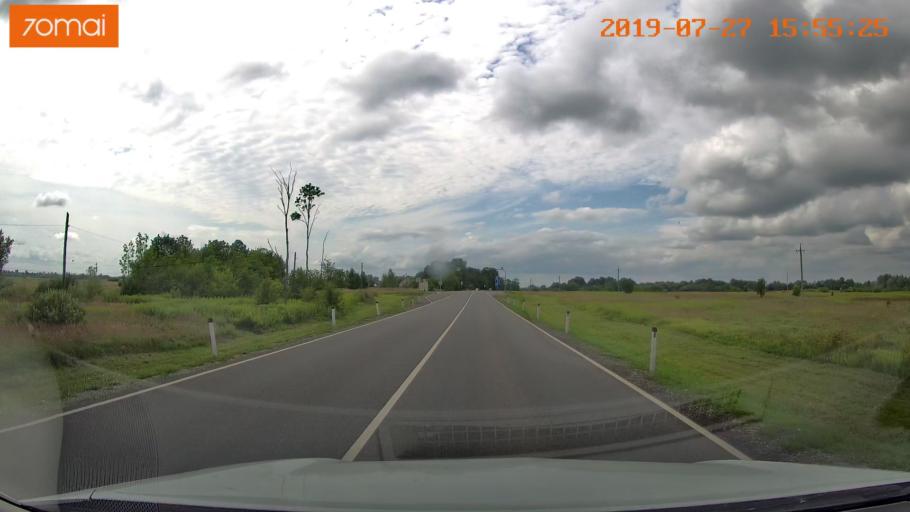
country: RU
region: Kaliningrad
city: Chernyakhovsk
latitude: 54.6137
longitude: 21.9210
